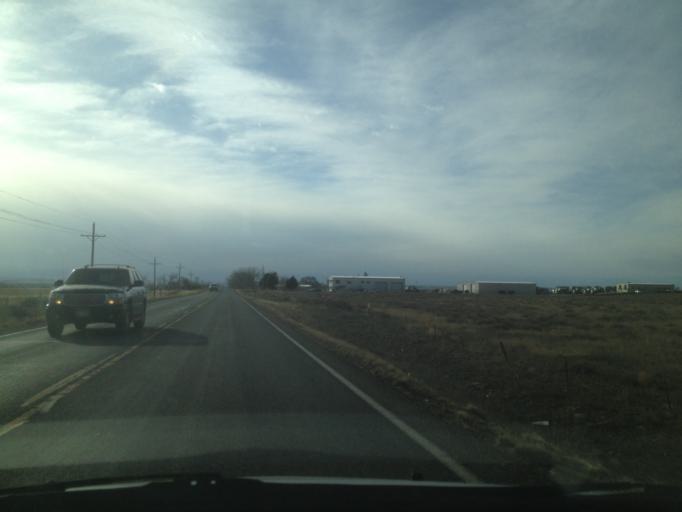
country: US
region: Colorado
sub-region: Weld County
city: Aristocrat Ranchettes
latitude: 40.0803
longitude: -104.7582
